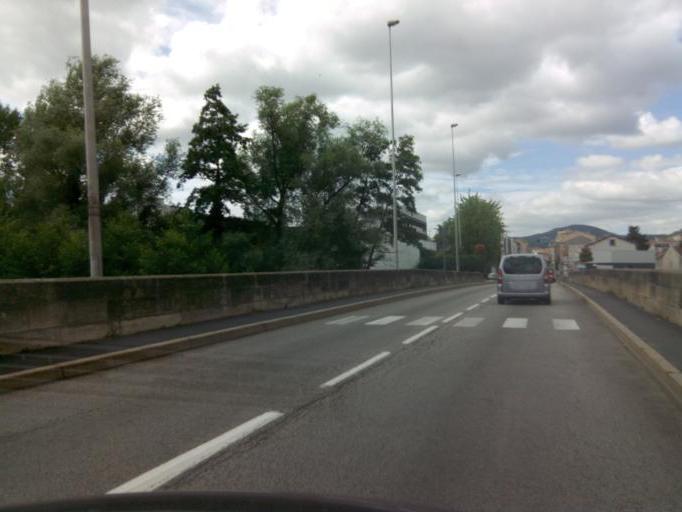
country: FR
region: Auvergne
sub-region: Departement de la Haute-Loire
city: Le Puy-en-Velay
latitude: 45.0508
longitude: 3.8959
